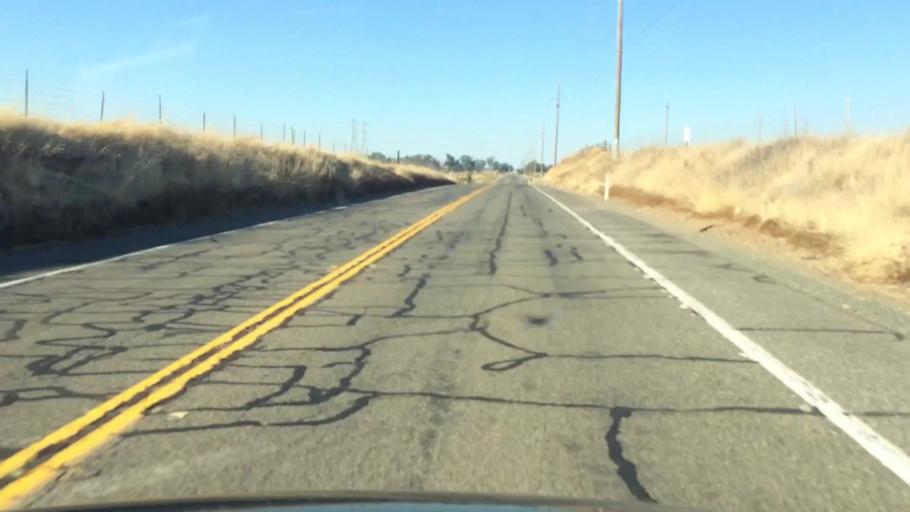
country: US
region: California
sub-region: Sacramento County
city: Clay
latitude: 38.3419
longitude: -121.1684
